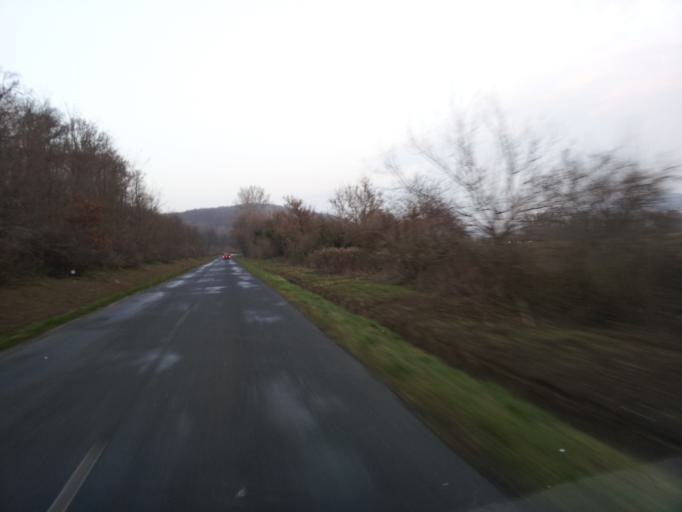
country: HU
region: Zala
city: Heviz
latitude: 46.8762
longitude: 17.1485
